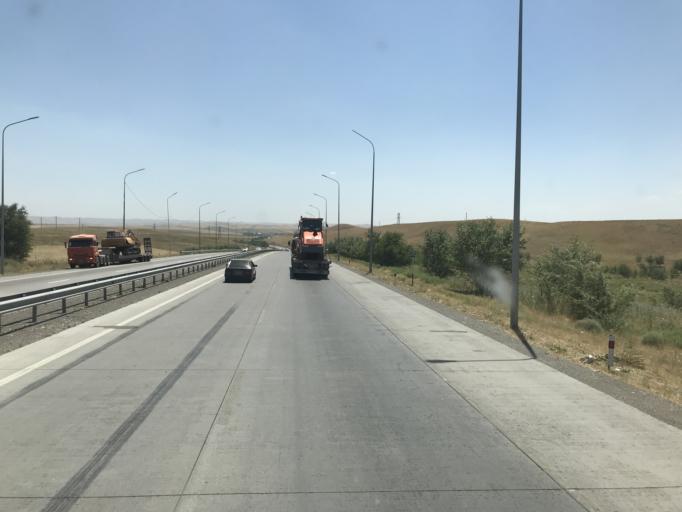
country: KZ
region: Ongtustik Qazaqstan
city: Shymkent
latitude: 42.2375
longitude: 69.5372
